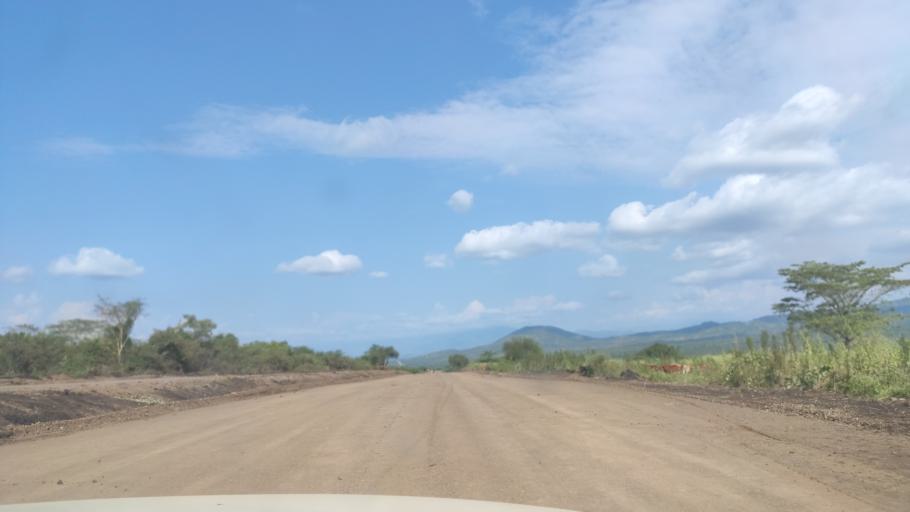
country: ET
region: Southern Nations, Nationalities, and People's Region
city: Felege Neway
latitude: 6.3981
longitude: 37.1150
